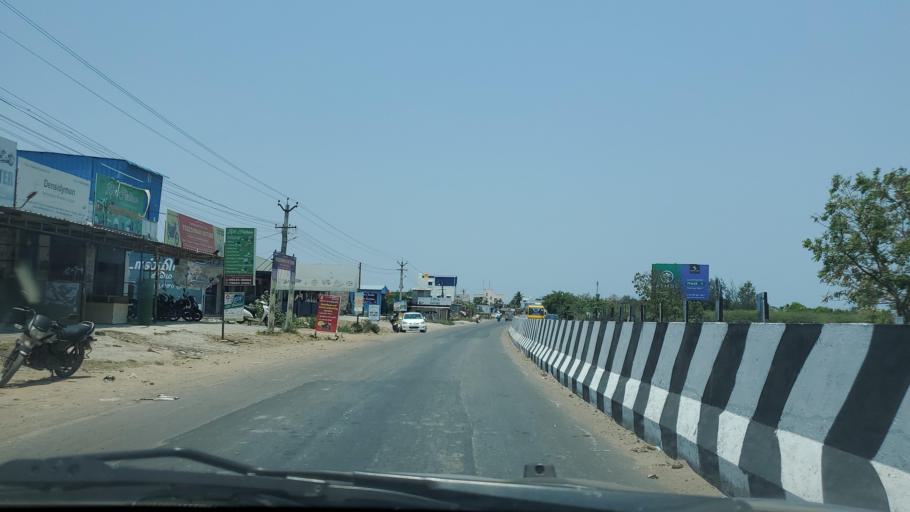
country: IN
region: Tamil Nadu
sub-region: Kancheepuram
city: Vengavasal
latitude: 12.8624
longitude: 80.1741
